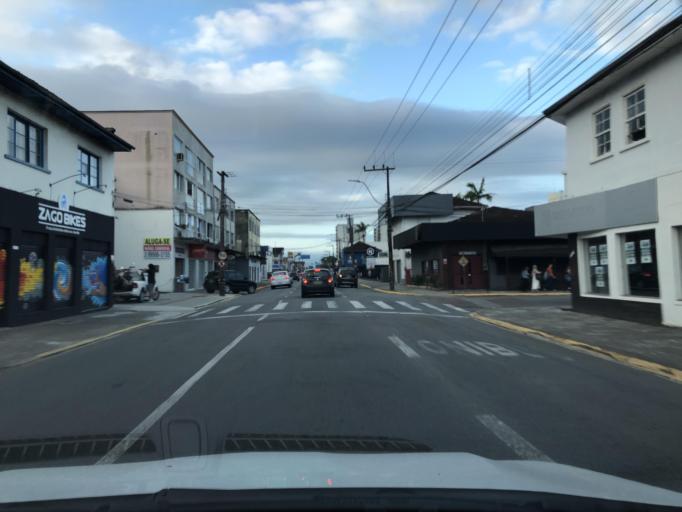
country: BR
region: Santa Catarina
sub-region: Joinville
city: Joinville
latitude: -26.2864
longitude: -48.8489
